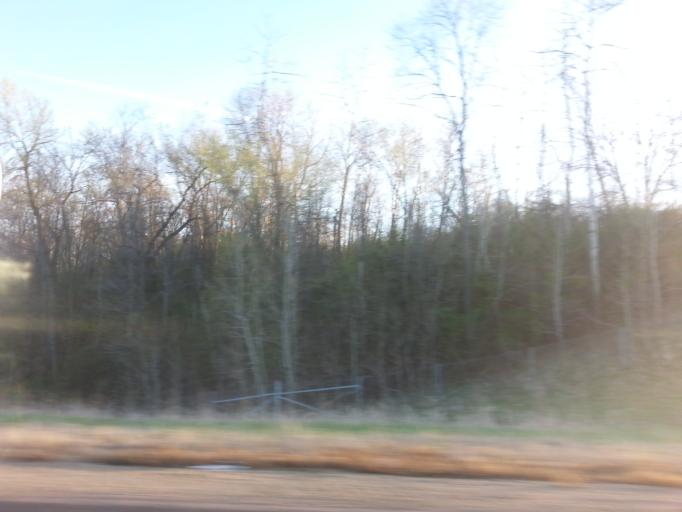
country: US
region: Minnesota
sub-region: Dakota County
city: Hastings
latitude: 44.7616
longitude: -92.8482
